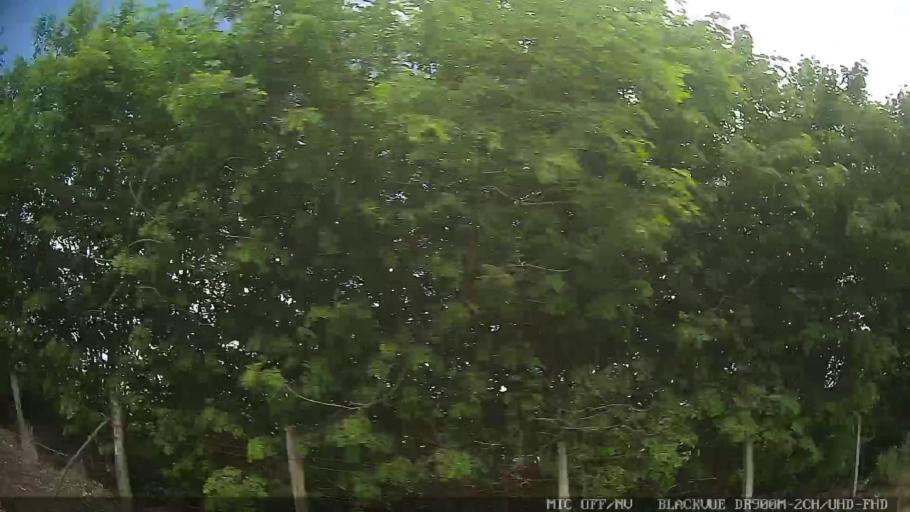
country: BR
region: Sao Paulo
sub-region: Conchas
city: Conchas
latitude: -22.9804
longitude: -47.9892
